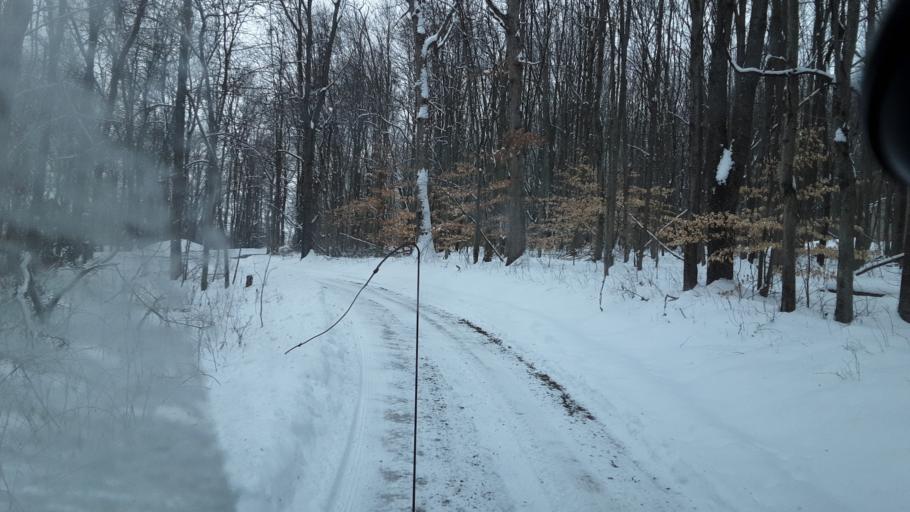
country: US
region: Ohio
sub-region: Perry County
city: Thornport
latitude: 39.9603
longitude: -82.3391
